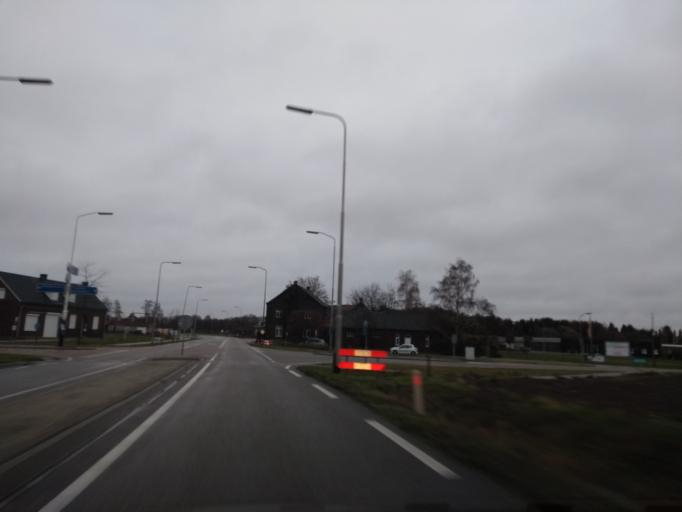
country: NL
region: Limburg
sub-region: Gemeente Weert
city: Weert
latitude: 51.2118
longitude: 5.7219
